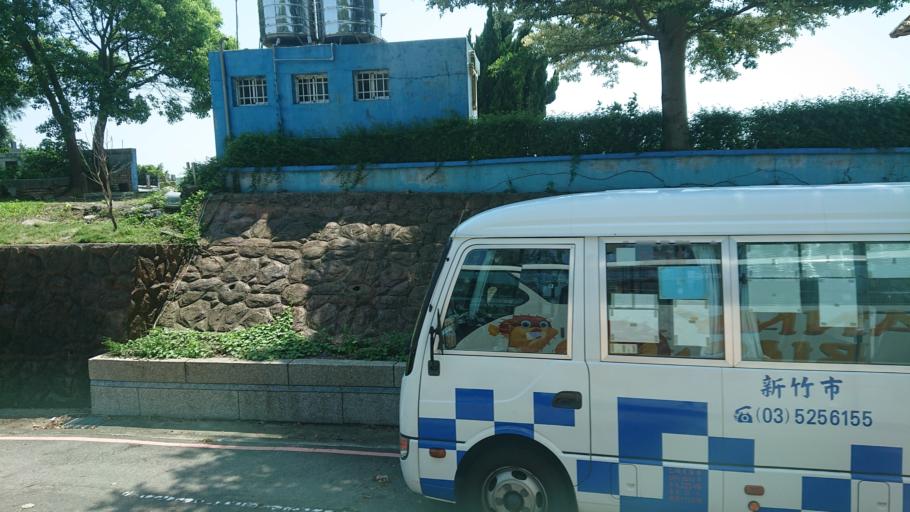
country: TW
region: Taiwan
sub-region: Hsinchu
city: Hsinchu
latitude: 24.7883
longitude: 120.9697
